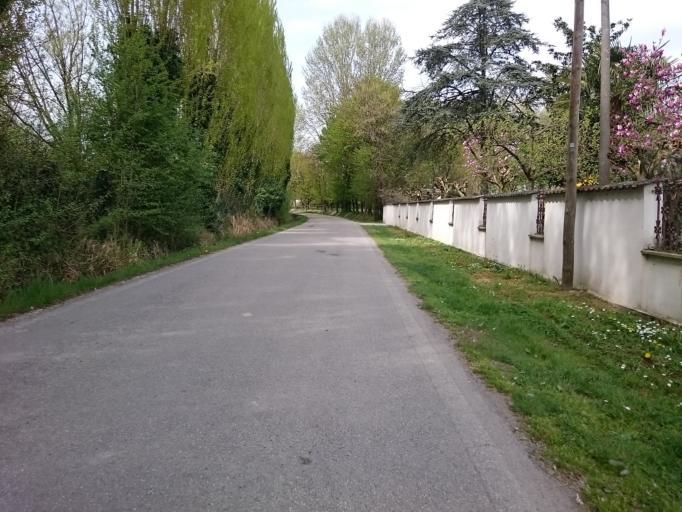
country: IT
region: Veneto
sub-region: Provincia di Padova
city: Tribano
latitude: 45.1934
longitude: 11.8280
